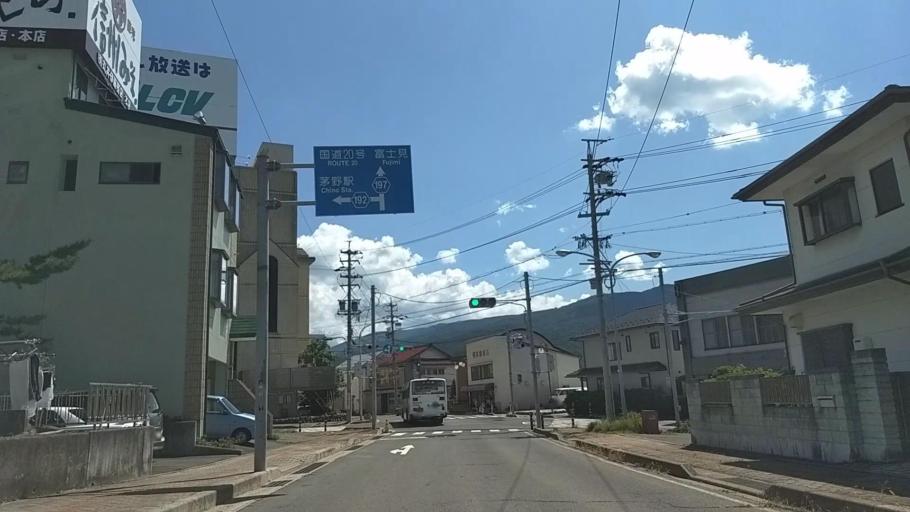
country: JP
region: Nagano
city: Chino
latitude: 35.9947
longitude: 138.1507
